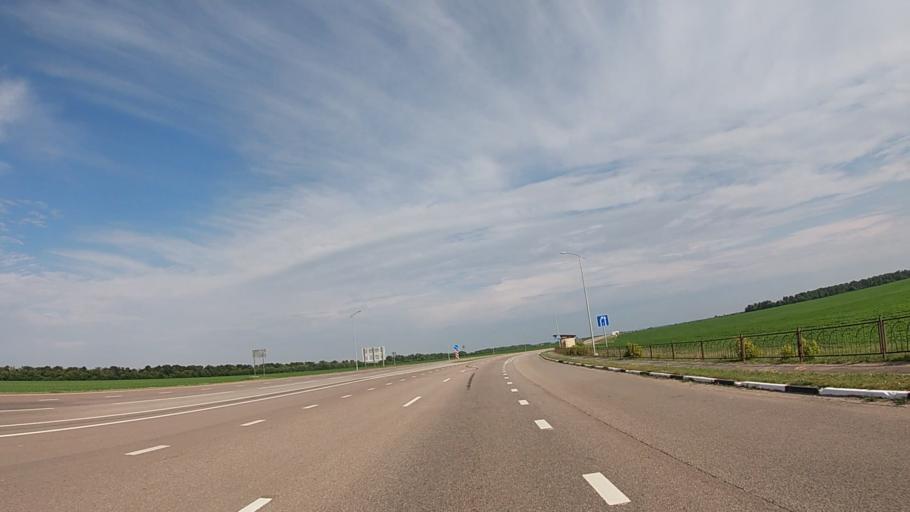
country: RU
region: Belgorod
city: Rakitnoye
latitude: 50.7917
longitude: 35.8667
